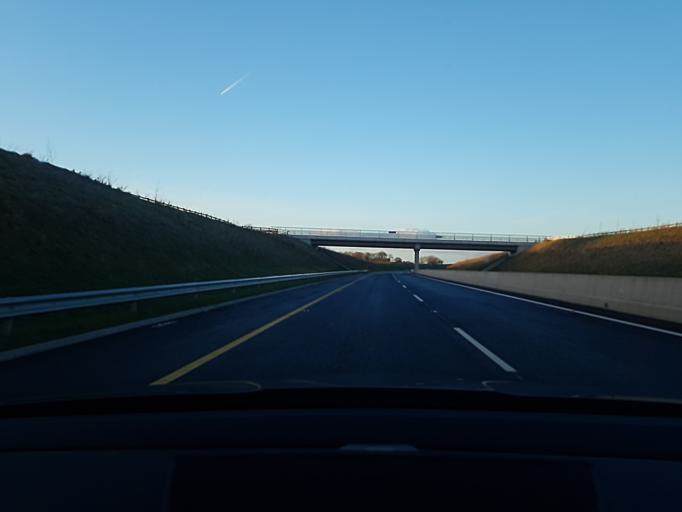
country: IE
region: Connaught
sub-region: County Galway
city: Tuam
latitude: 53.4379
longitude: -8.8467
